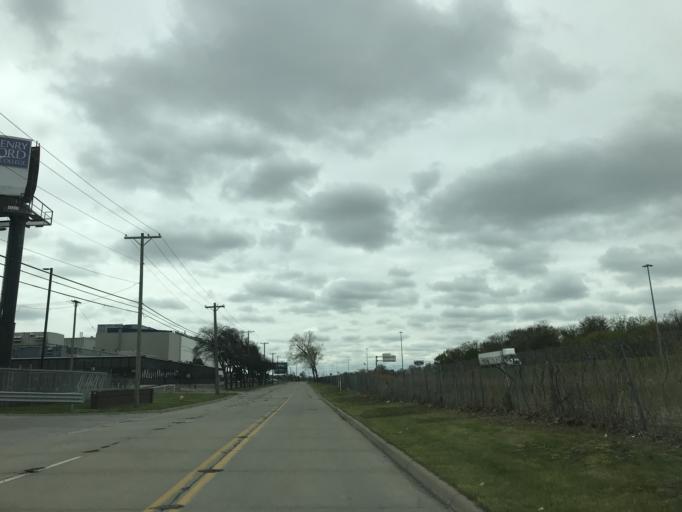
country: US
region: Michigan
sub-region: Wayne County
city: Melvindale
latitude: 42.2920
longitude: -83.1893
